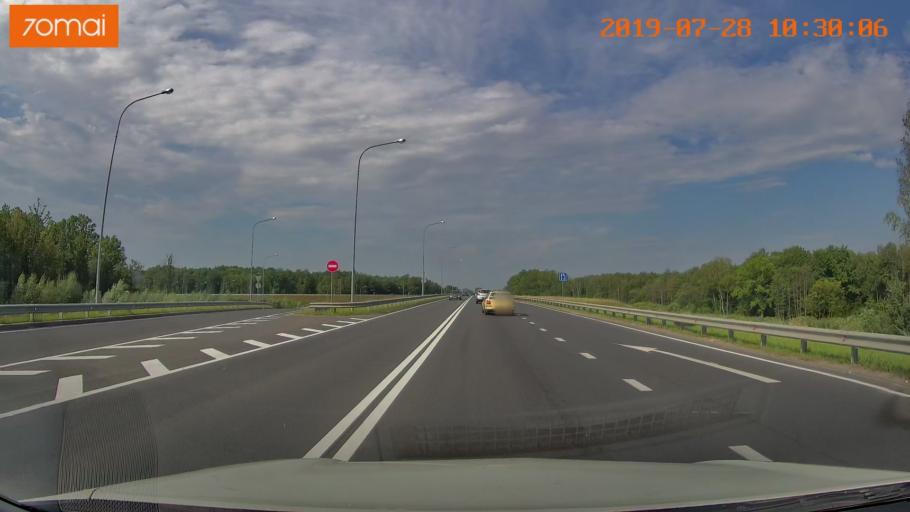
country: RU
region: Kaliningrad
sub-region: Gorod Kaliningrad
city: Kaliningrad
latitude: 54.7642
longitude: 20.4734
